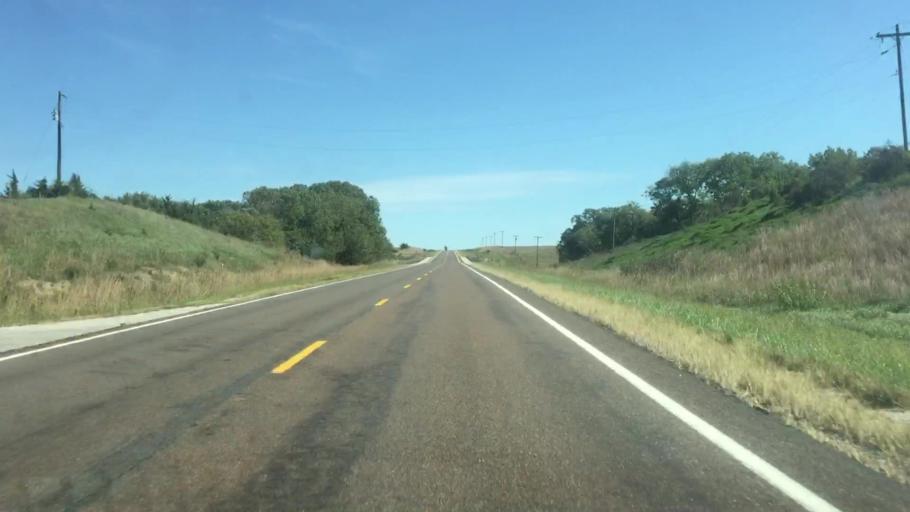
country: US
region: Nebraska
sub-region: Gage County
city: Wymore
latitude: 40.0454
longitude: -96.7762
